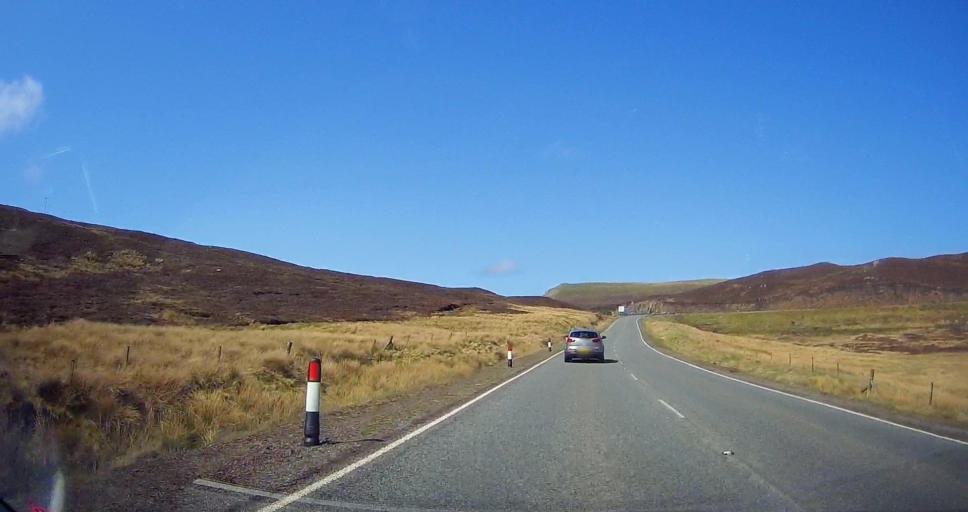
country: GB
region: Scotland
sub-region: Shetland Islands
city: Lerwick
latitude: 60.1411
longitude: -1.2407
